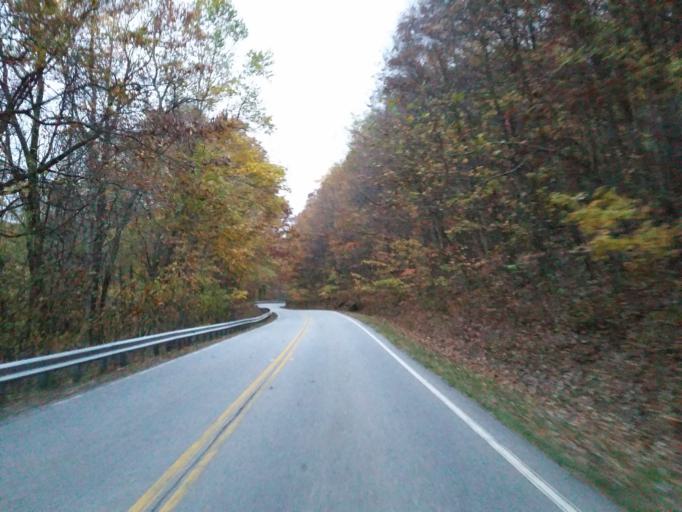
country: US
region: Georgia
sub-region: Lumpkin County
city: Dahlonega
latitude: 34.6828
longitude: -84.0054
